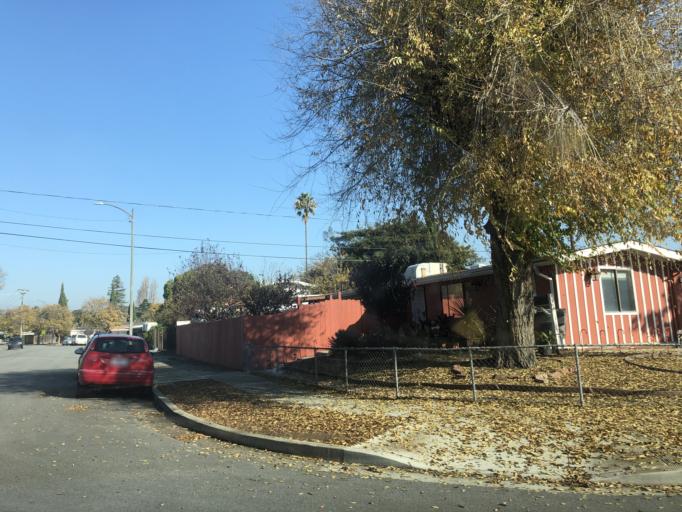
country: US
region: California
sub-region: Santa Clara County
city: Sunnyvale
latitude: 37.3942
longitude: -122.0040
